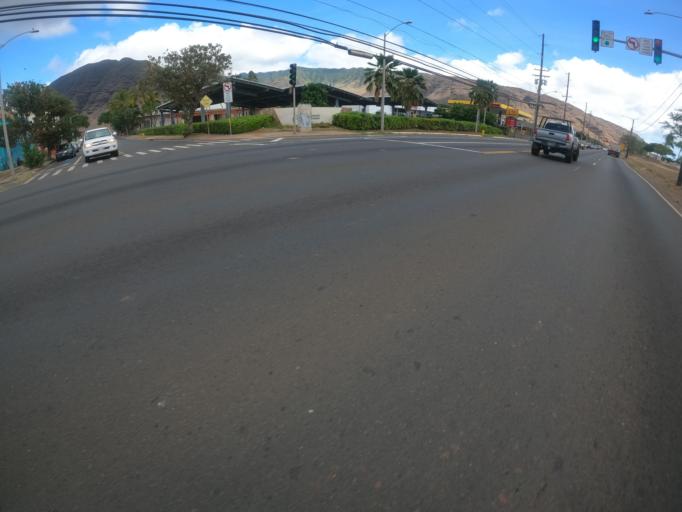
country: US
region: Hawaii
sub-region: Honolulu County
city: Nanakuli
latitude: 21.3858
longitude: -158.1502
